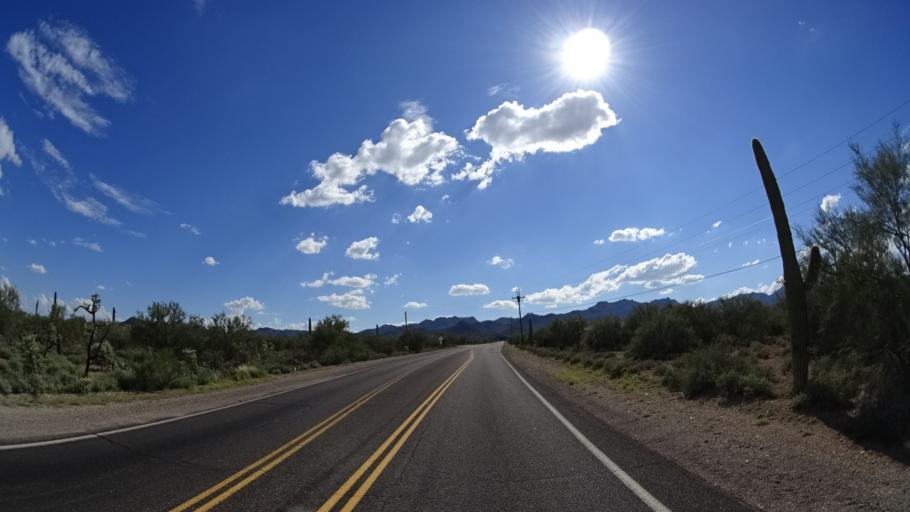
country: US
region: Arizona
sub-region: Pima County
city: Flowing Wells
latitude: 32.2777
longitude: -111.0571
